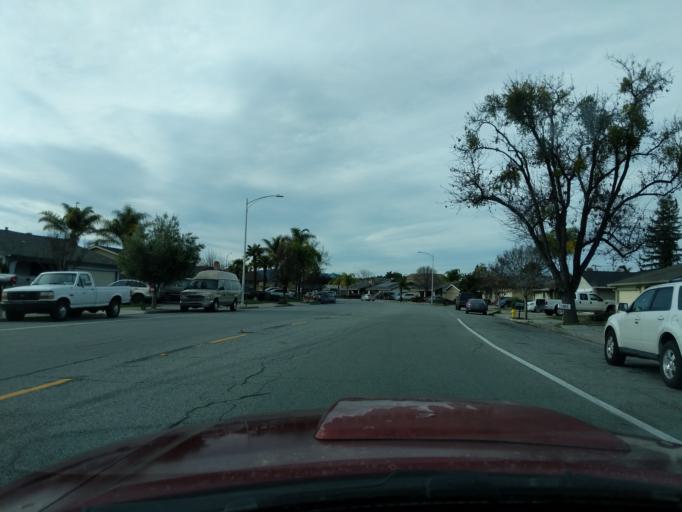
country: US
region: California
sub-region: Santa Clara County
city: Gilroy
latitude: 37.0170
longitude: -121.5875
